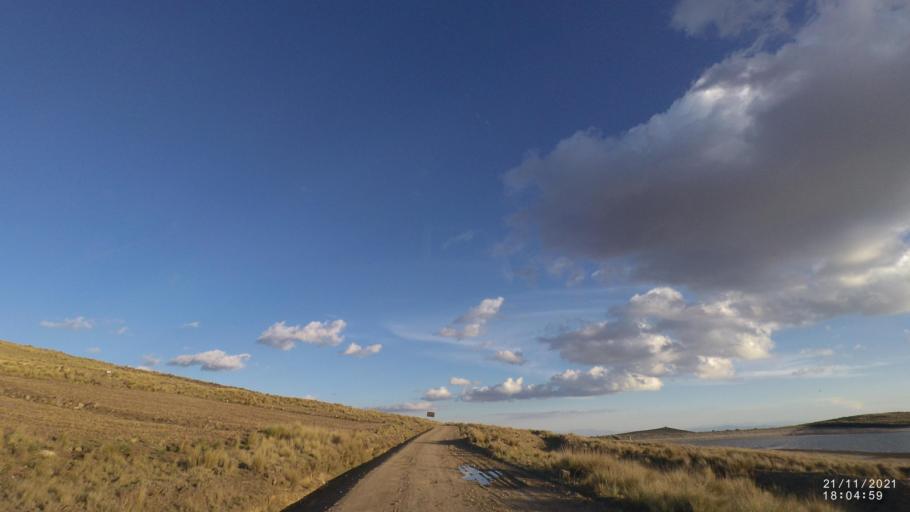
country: BO
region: Cochabamba
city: Cochabamba
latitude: -17.2697
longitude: -66.2189
